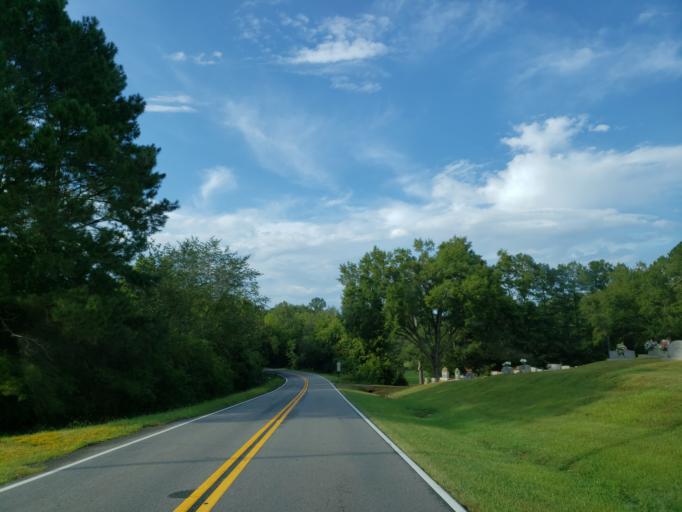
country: US
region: Georgia
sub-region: Bartow County
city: Euharlee
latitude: 34.1748
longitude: -84.9794
